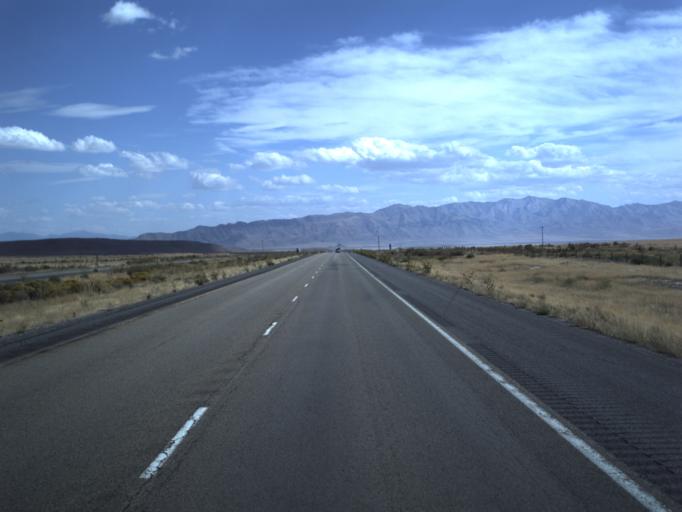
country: US
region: Utah
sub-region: Tooele County
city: Grantsville
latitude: 40.8020
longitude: -112.8534
